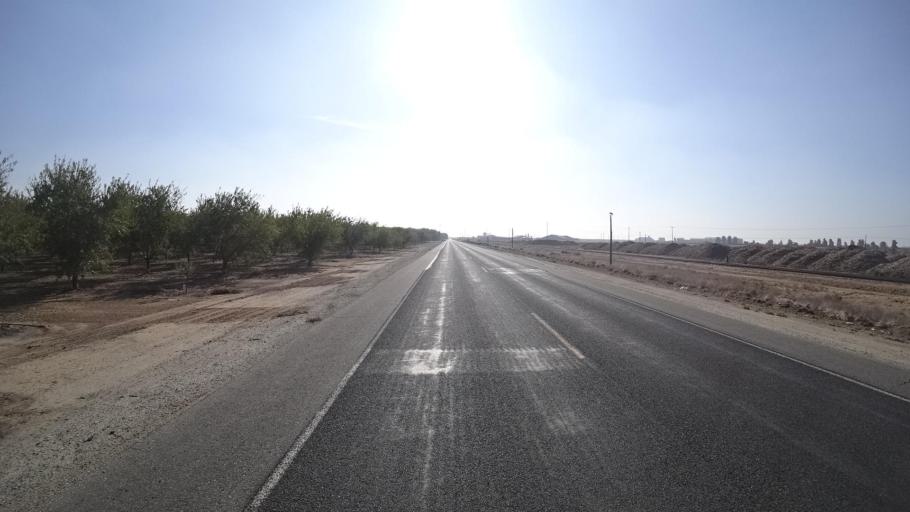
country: US
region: California
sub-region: Kern County
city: McFarland
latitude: 35.6409
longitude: -119.2028
